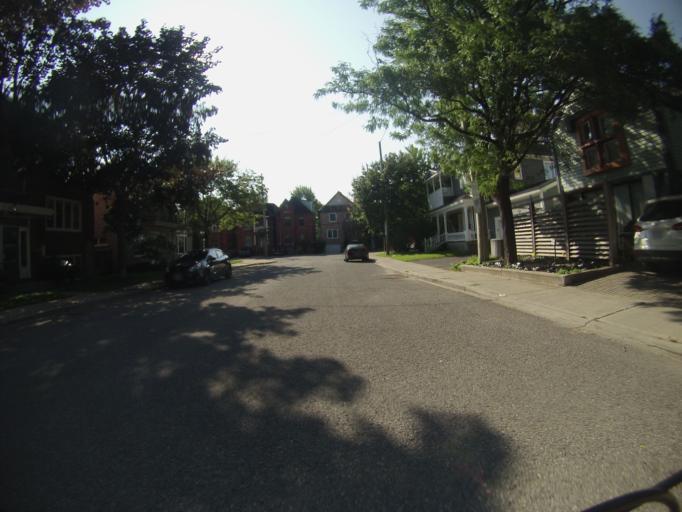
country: CA
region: Ontario
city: Ottawa
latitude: 45.4169
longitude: -75.6844
